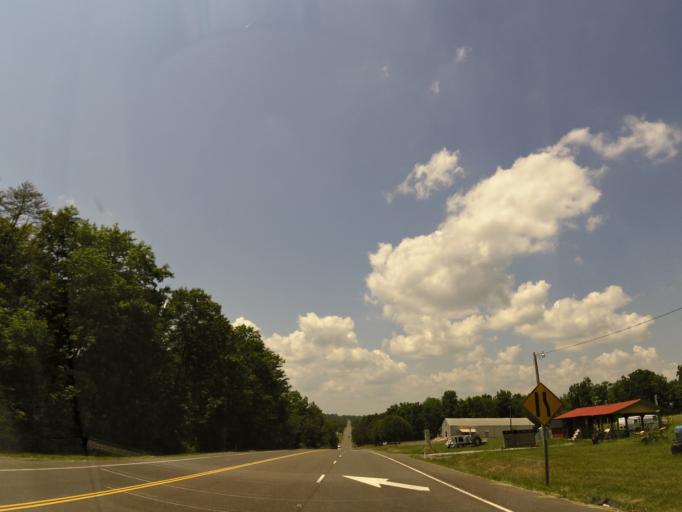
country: US
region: Tennessee
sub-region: Rhea County
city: Dayton
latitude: 35.5335
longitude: -85.0524
